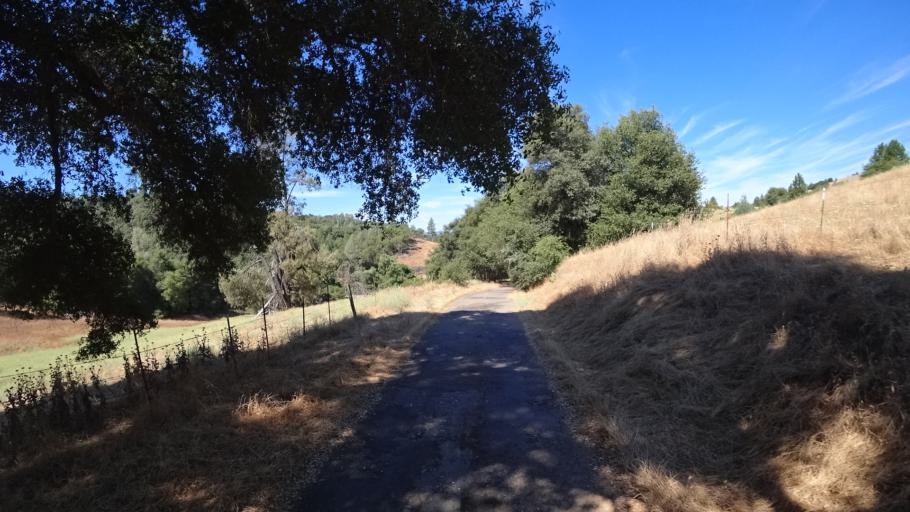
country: US
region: California
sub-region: Calaveras County
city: Angels Camp
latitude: 38.1428
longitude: -120.5356
